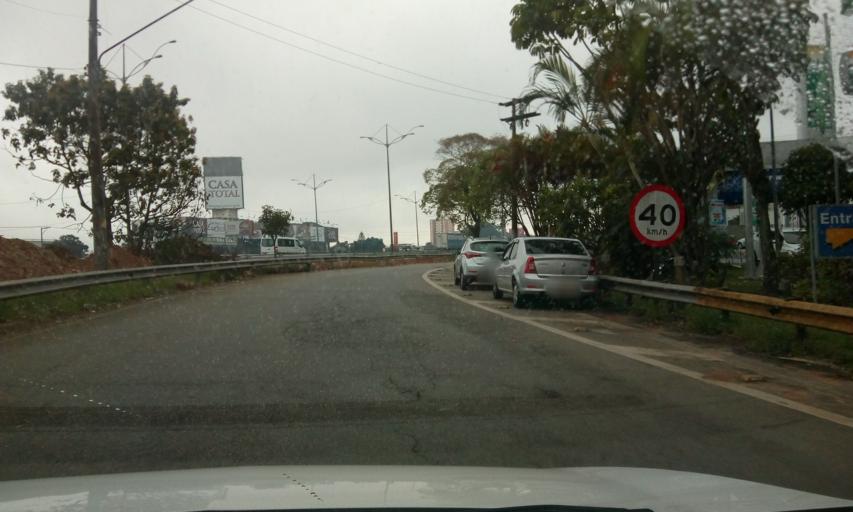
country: BR
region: Sao Paulo
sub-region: Sao Bernardo Do Campo
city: Sao Bernardo do Campo
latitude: -23.6876
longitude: -46.5648
